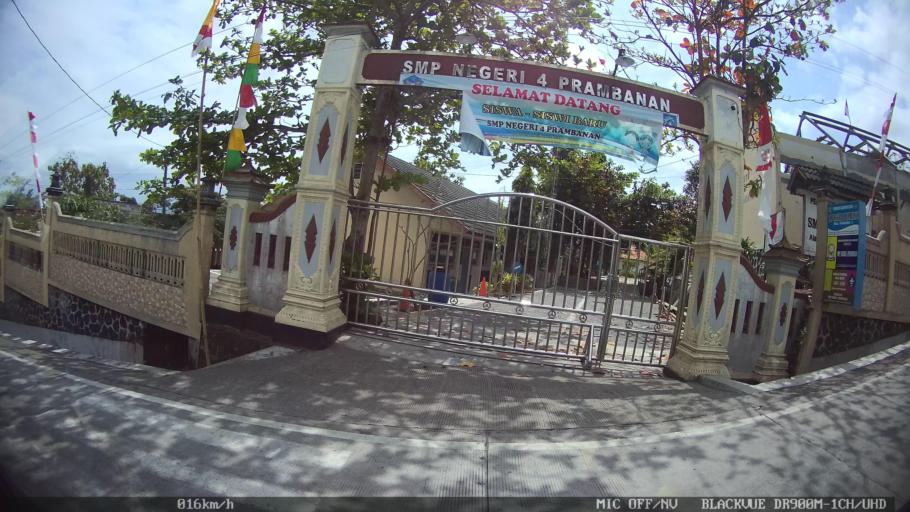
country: ID
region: Central Java
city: Candi Prambanan
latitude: -7.7837
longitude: 110.5067
